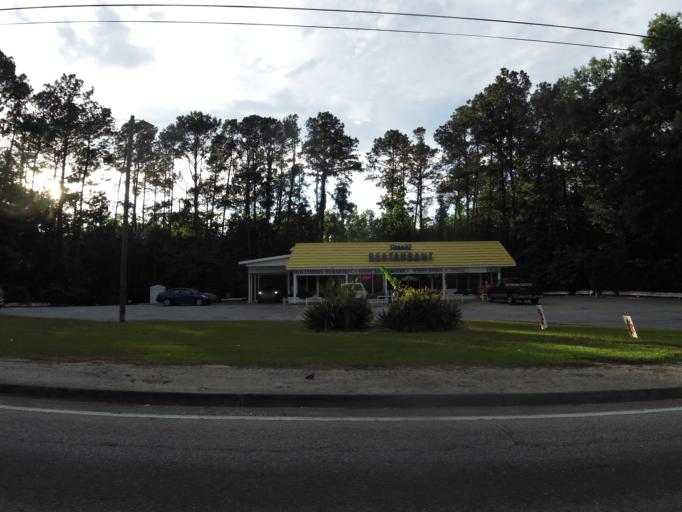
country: US
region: Georgia
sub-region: Chatham County
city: Pooler
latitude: 32.0711
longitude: -81.2017
